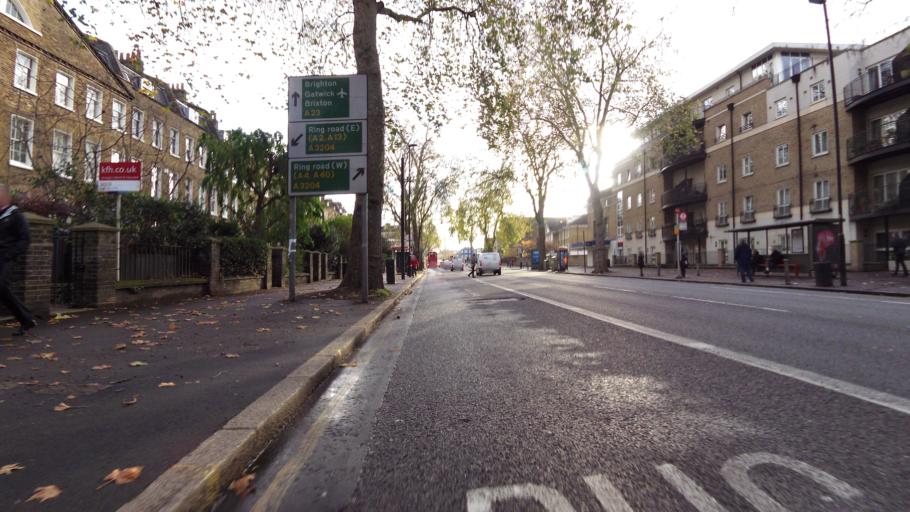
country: GB
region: England
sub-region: Greater London
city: Kennington
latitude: 51.4902
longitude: -0.1111
